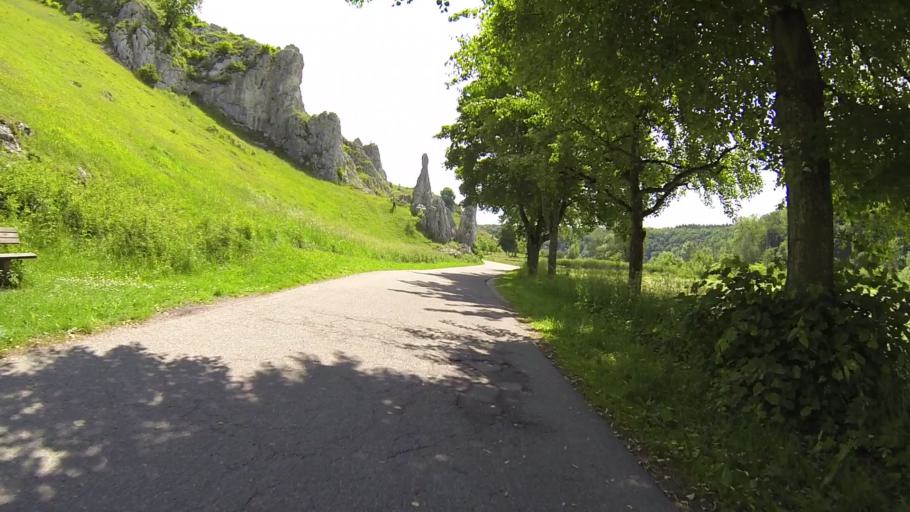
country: DE
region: Baden-Wuerttemberg
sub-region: Regierungsbezirk Stuttgart
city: Herbrechtingen
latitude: 48.6088
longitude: 10.1781
